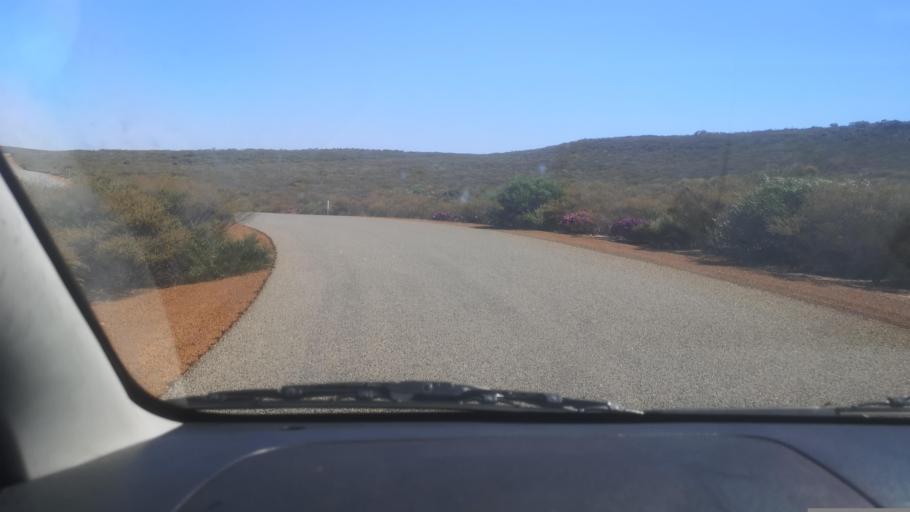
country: AU
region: Western Australia
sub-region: Northampton Shire
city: Kalbarri
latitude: -27.8117
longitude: 114.4703
